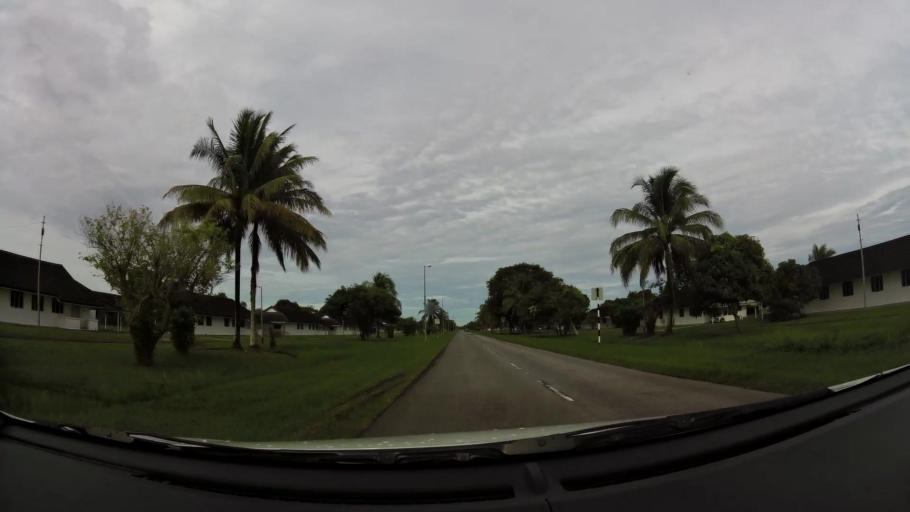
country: BN
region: Belait
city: Seria
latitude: 4.6106
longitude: 114.3267
